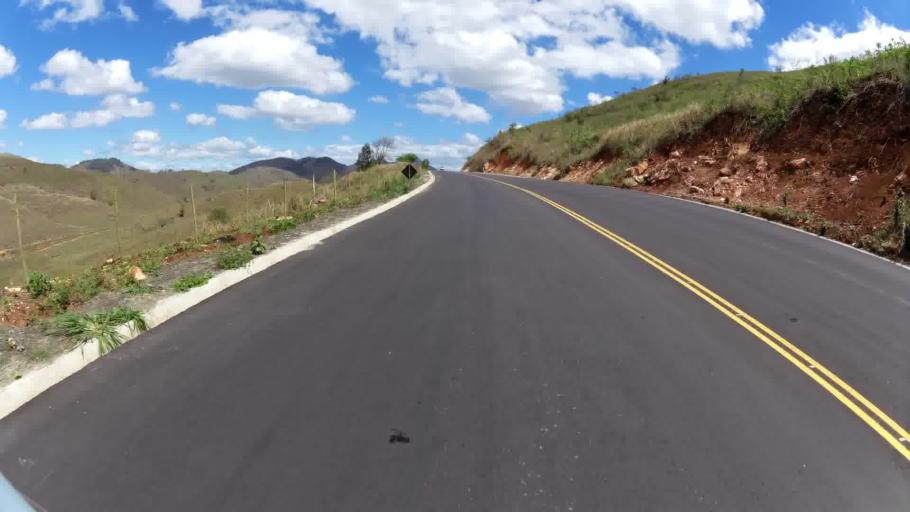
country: BR
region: Rio de Janeiro
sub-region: Itaperuna
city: Itaperuna
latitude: -21.2852
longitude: -41.7979
